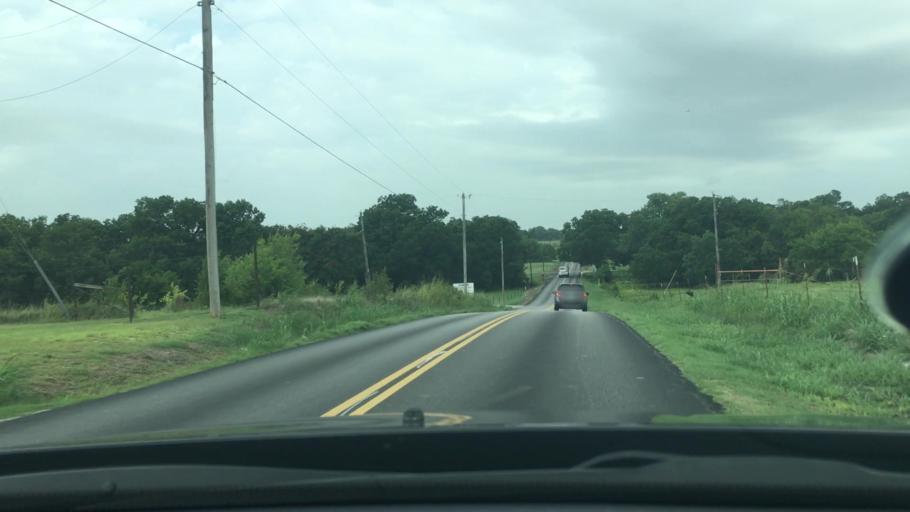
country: US
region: Oklahoma
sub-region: Carter County
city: Lone Grove
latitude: 34.2020
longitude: -97.2046
